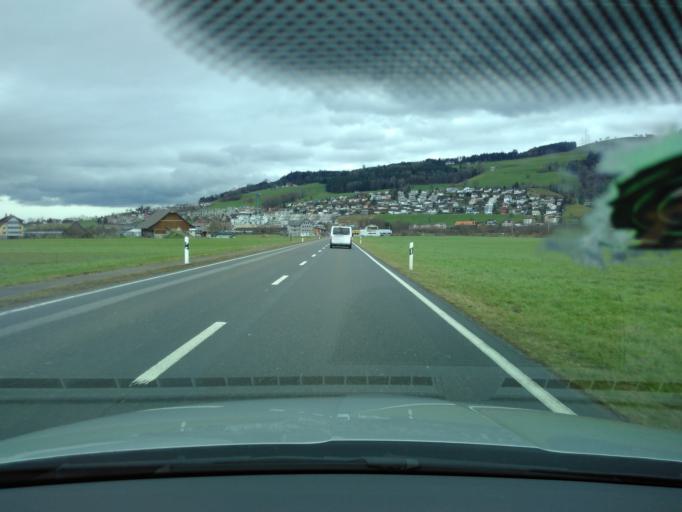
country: CH
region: Lucerne
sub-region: Lucerne-Land District
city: Root
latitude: 47.1248
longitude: 8.3837
